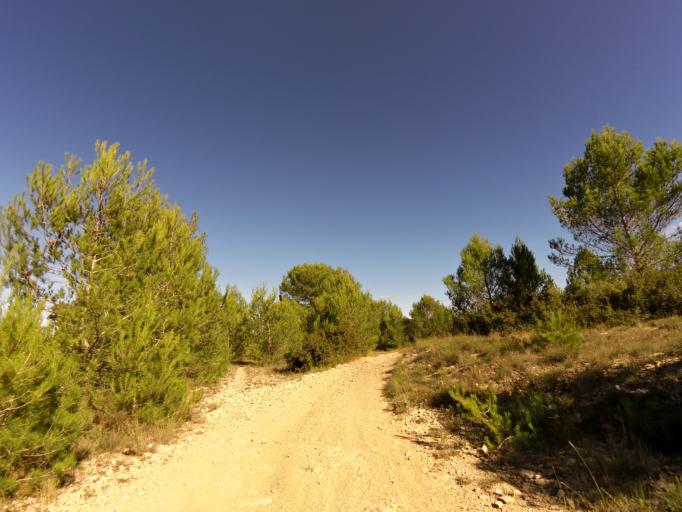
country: FR
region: Languedoc-Roussillon
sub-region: Departement de l'Herault
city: Villetelle
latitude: 43.7369
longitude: 4.1510
